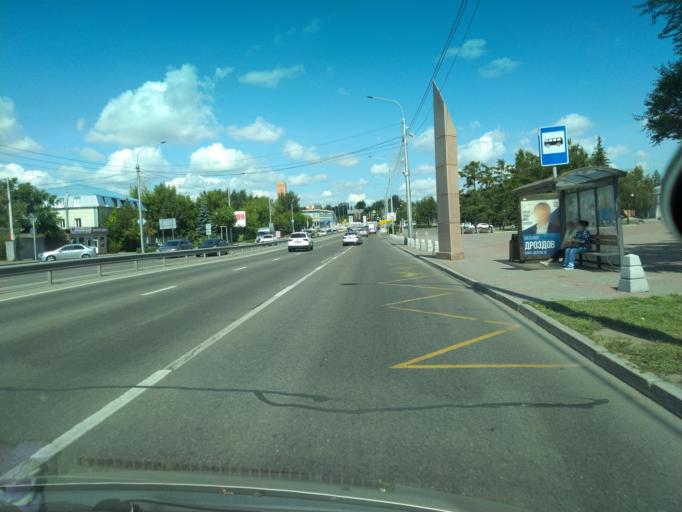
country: RU
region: Krasnoyarskiy
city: Krasnoyarsk
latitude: 56.0218
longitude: 92.8853
